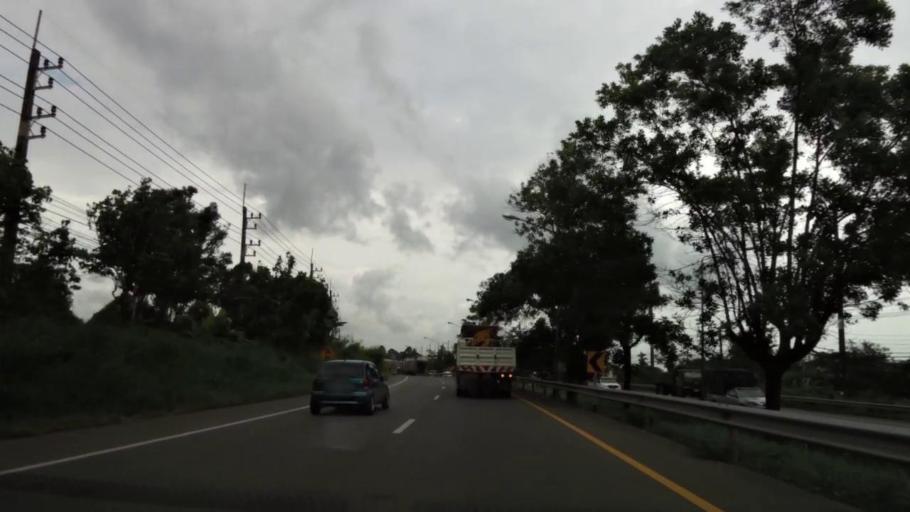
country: TH
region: Chanthaburi
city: Tha Mai
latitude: 12.7187
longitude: 101.9763
